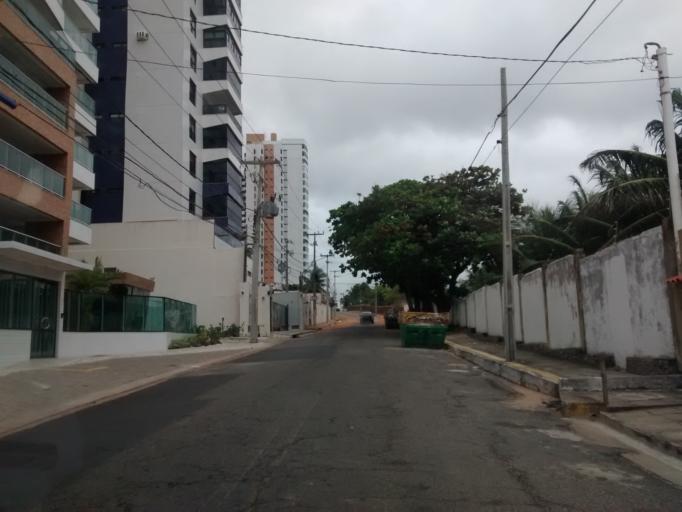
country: BR
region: Rio Grande do Norte
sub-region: Natal
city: Natal
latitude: -5.7856
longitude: -35.1914
